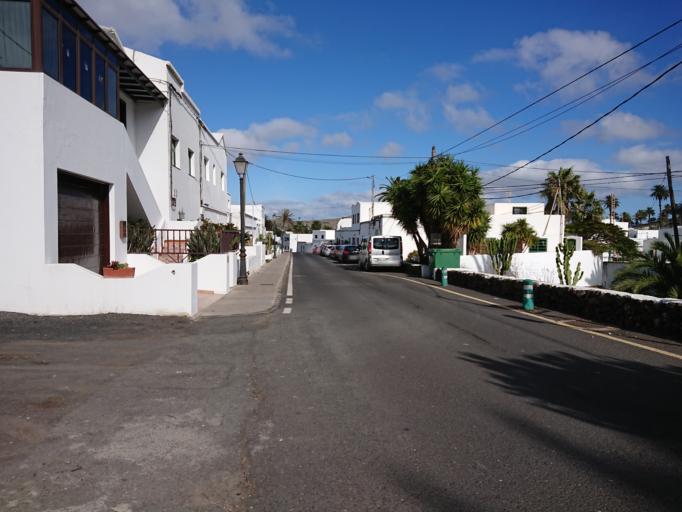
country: ES
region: Canary Islands
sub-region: Provincia de Las Palmas
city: Haria
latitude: 29.1431
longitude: -13.5034
